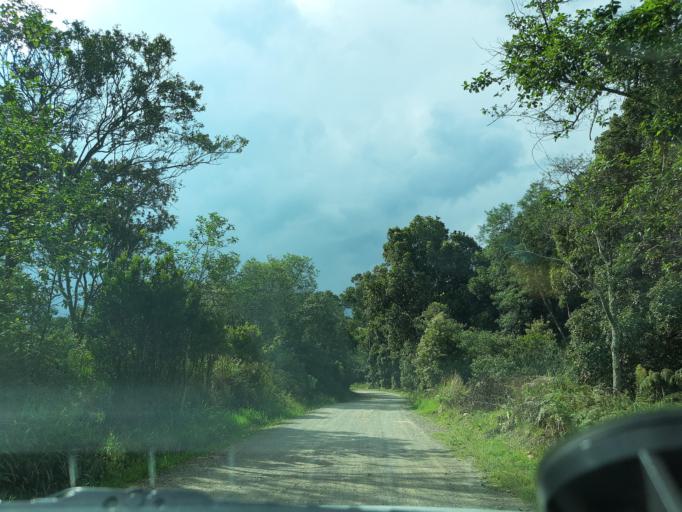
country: CO
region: Boyaca
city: Raquira
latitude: 5.5161
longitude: -73.6669
